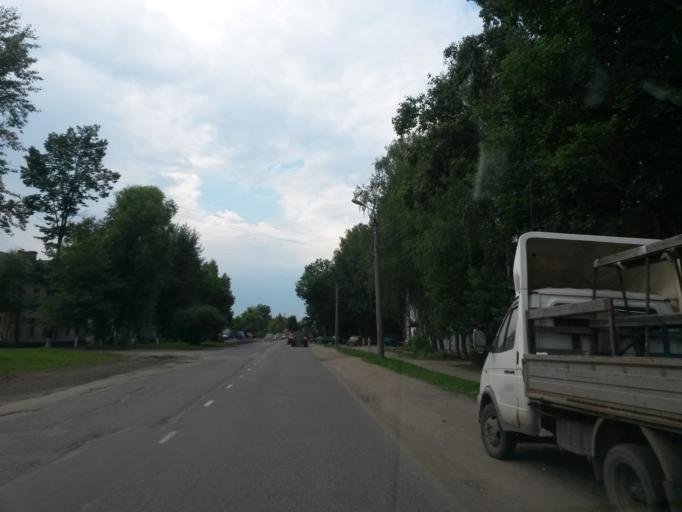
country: RU
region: Jaroslavl
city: Yaroslavl
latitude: 57.6062
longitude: 39.8149
